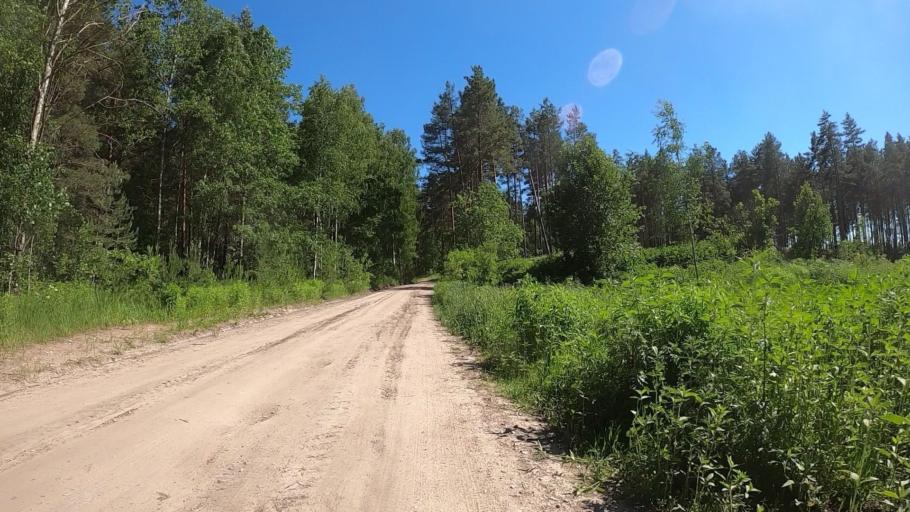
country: LV
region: Stopini
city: Ulbroka
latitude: 56.8845
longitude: 24.3013
